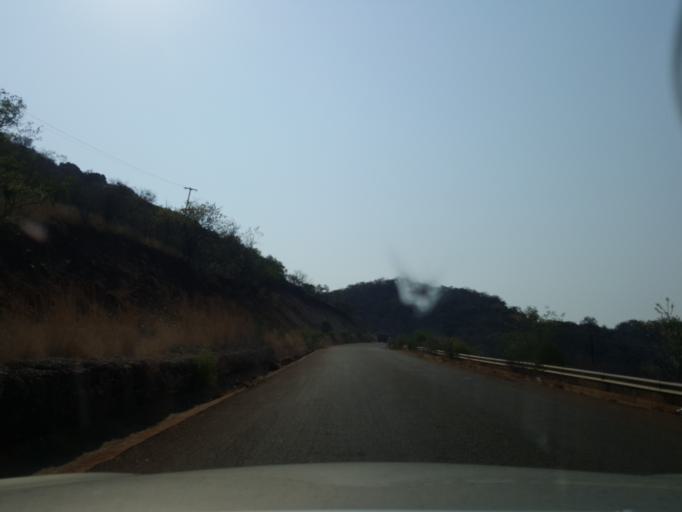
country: BW
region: South East
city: Lobatse
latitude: -25.2846
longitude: 25.8687
